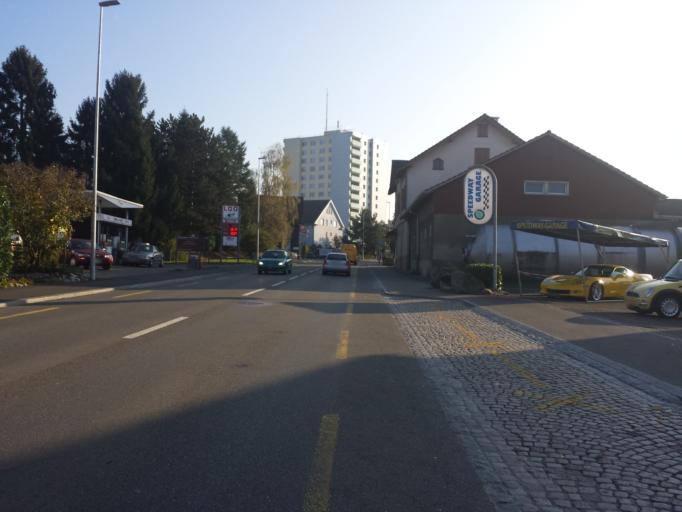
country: CH
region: Thurgau
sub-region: Arbon District
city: Salmsach
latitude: 47.5685
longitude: 9.3664
